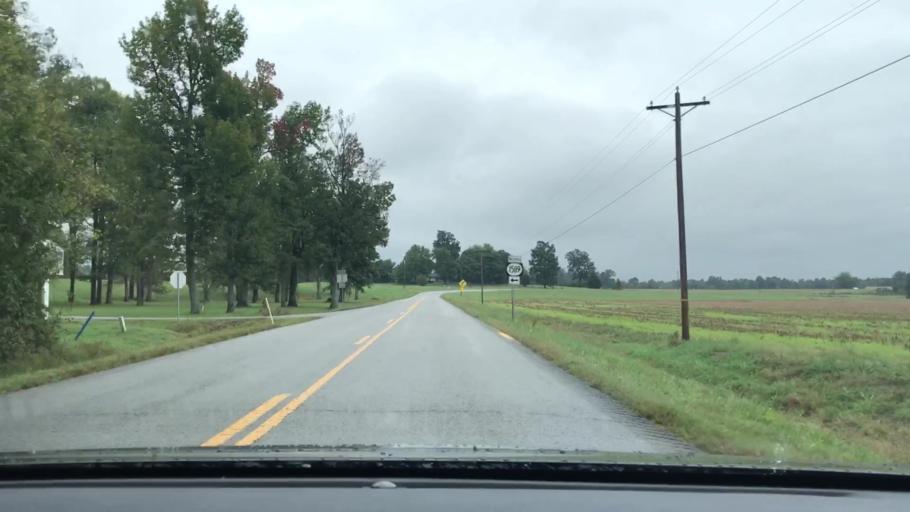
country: US
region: Kentucky
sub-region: McLean County
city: Calhoun
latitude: 37.4716
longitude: -87.2366
